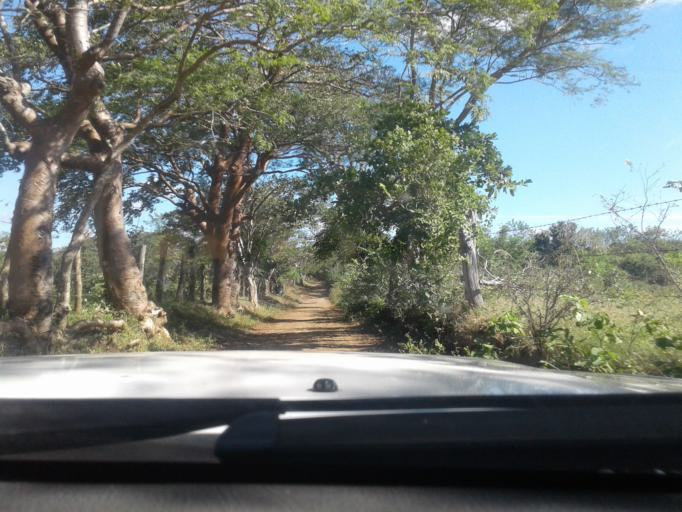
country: NI
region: Carazo
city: Santa Teresa
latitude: 11.7483
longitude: -86.1827
